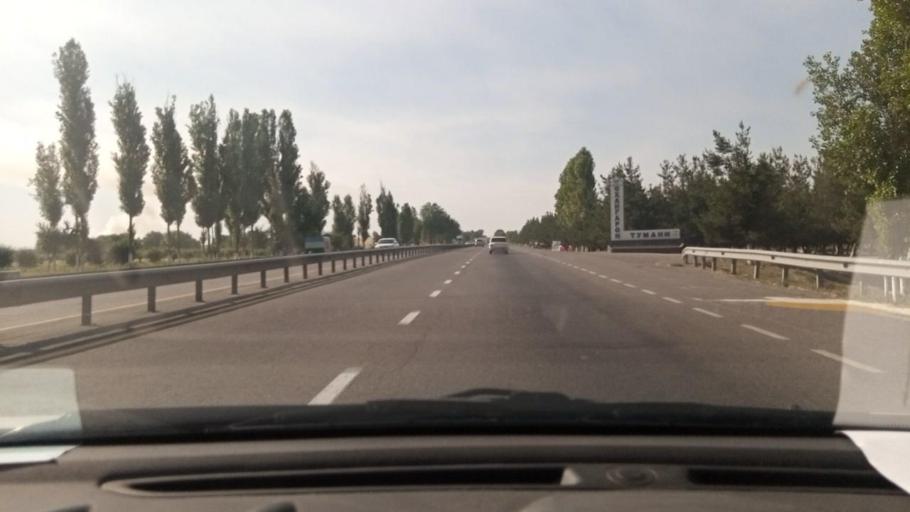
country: UZ
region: Toshkent
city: Tuytepa
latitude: 41.1181
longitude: 69.4435
